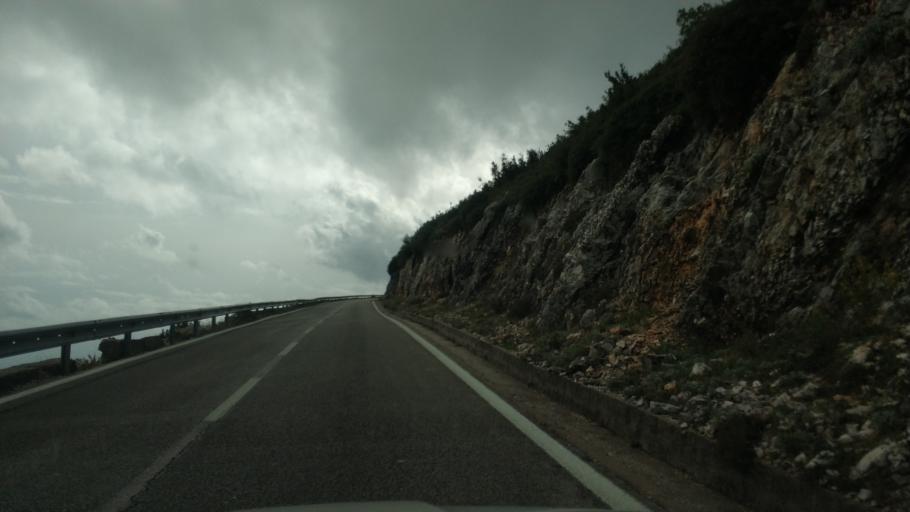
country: AL
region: Vlore
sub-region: Rrethi i Vlores
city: Vranisht
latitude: 40.1842
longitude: 19.6045
